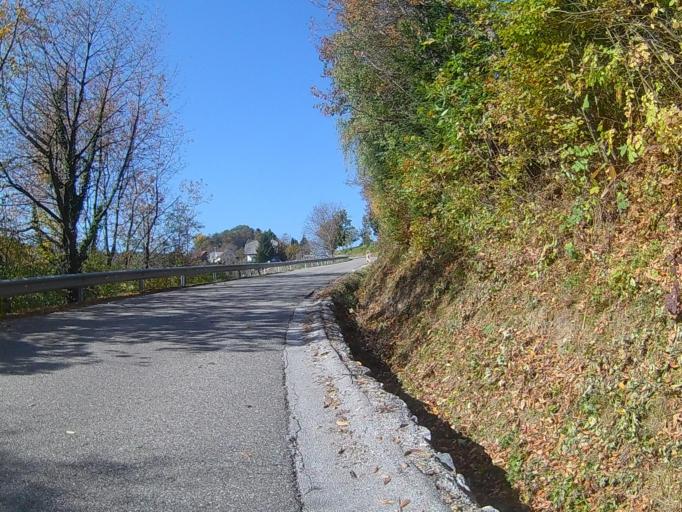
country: SI
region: Race-Fram
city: Fram
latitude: 46.4585
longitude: 15.6213
